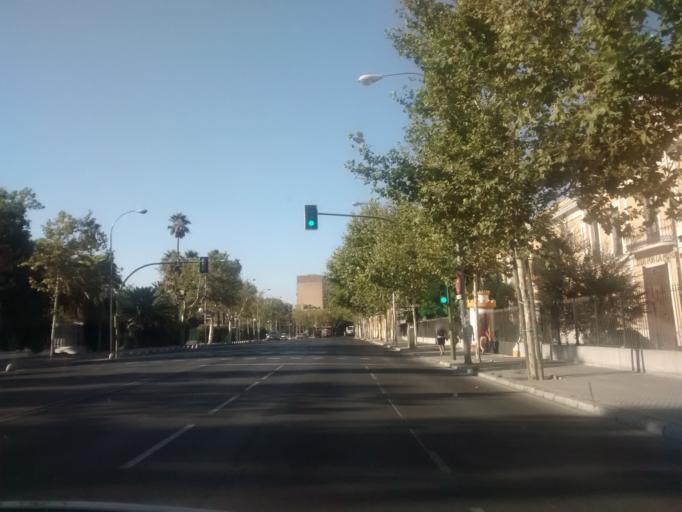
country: ES
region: Andalusia
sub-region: Provincia de Sevilla
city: Sevilla
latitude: 37.3753
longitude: -5.9848
